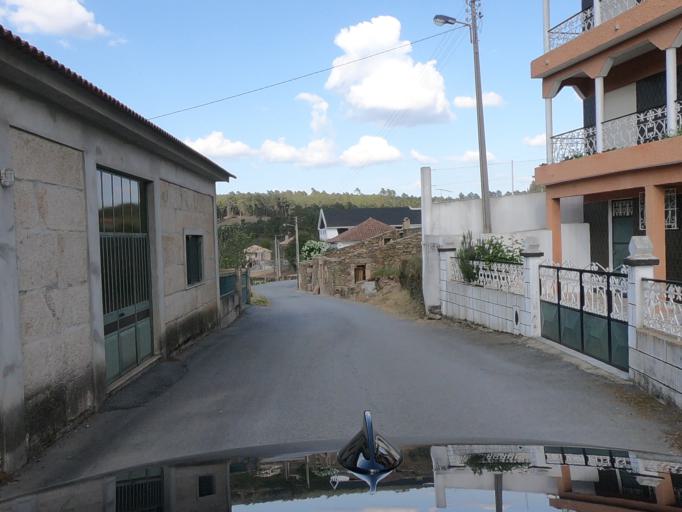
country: PT
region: Vila Real
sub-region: Sabrosa
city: Vilela
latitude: 41.2416
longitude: -7.6544
